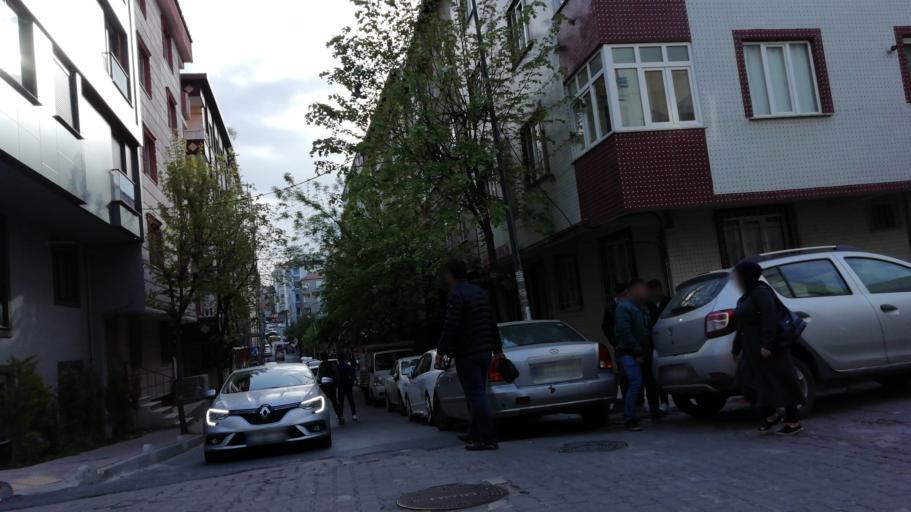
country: TR
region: Istanbul
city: Bagcilar
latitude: 41.0219
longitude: 28.8355
